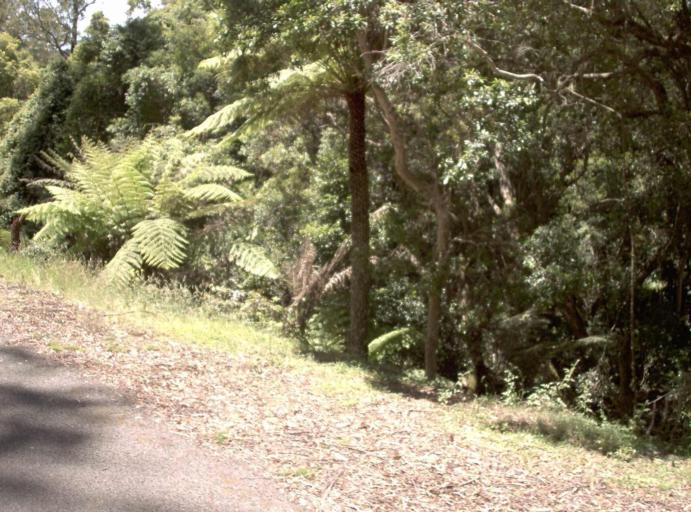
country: AU
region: New South Wales
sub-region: Bombala
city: Bombala
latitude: -37.4680
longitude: 148.9327
